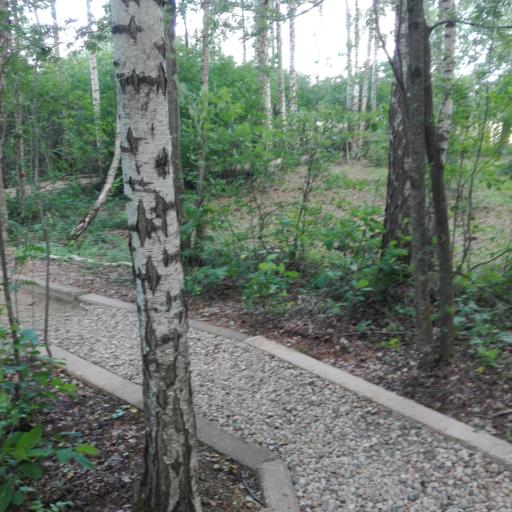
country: LT
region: Panevezys
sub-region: Birzai
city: Birzai
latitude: 56.2338
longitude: 24.7831
